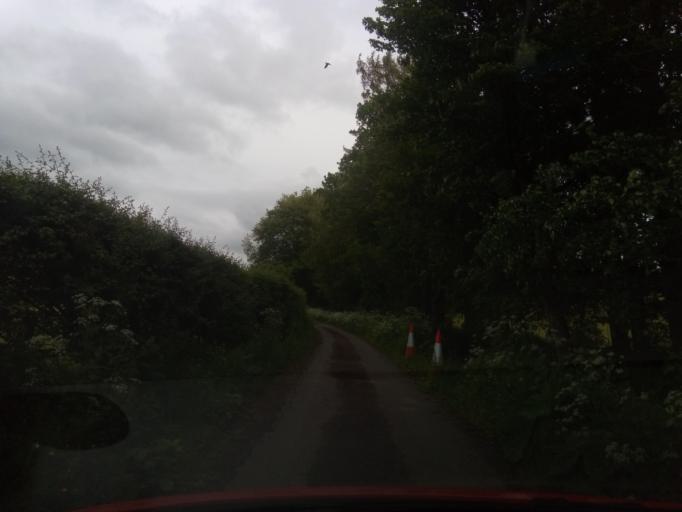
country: GB
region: Scotland
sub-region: The Scottish Borders
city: Selkirk
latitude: 55.5675
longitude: -2.8210
